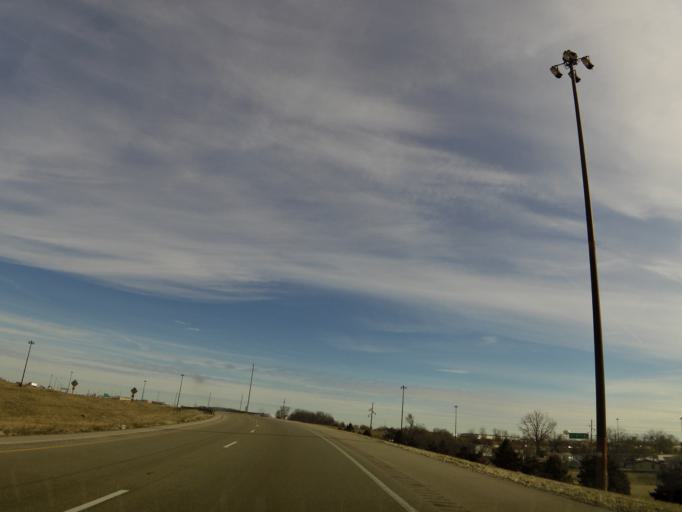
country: US
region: Illinois
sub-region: McLean County
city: Normal
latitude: 40.5370
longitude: -89.0039
